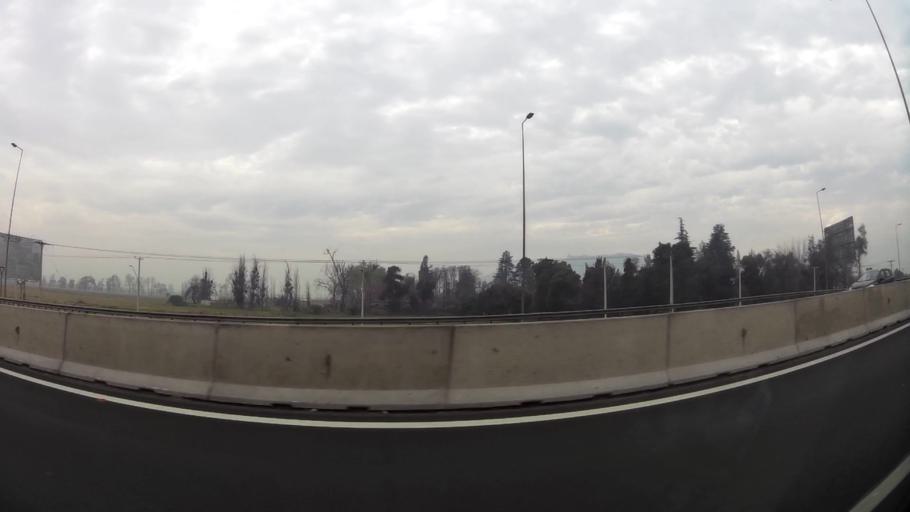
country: CL
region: Santiago Metropolitan
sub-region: Provincia de Santiago
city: Lo Prado
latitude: -33.4116
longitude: -70.7481
